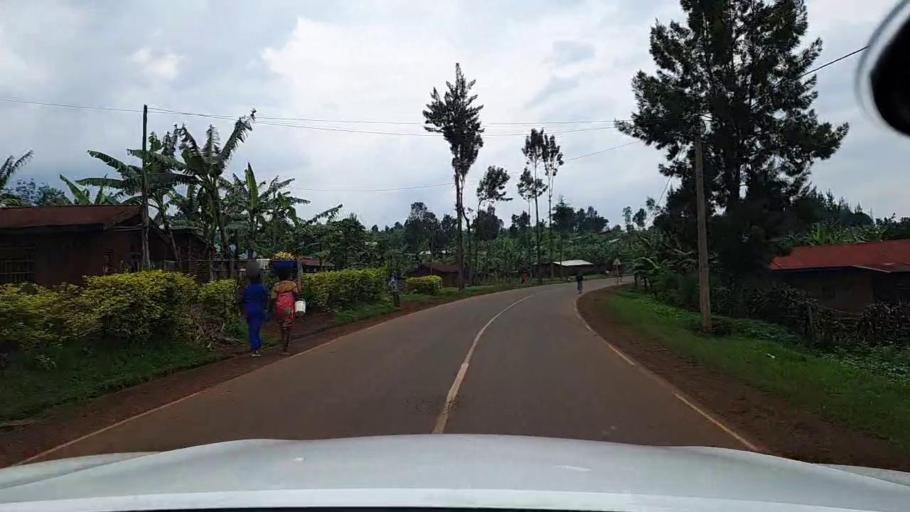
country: RW
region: Western Province
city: Cyangugu
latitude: -2.6145
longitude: 28.9436
